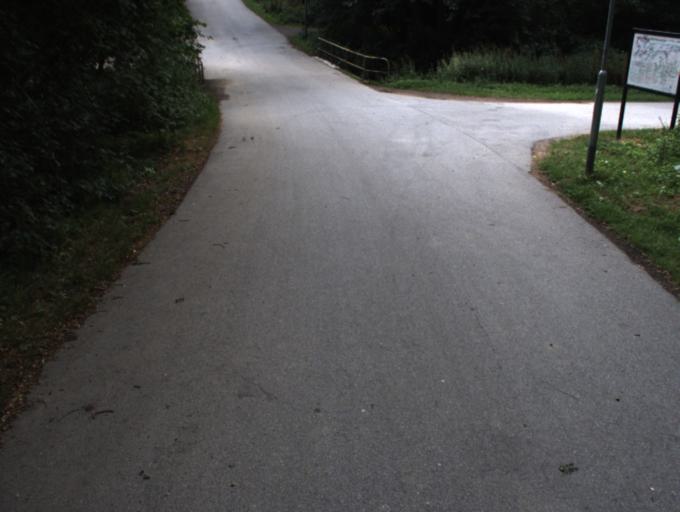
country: SE
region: Skane
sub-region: Helsingborg
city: Helsingborg
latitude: 56.0340
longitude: 12.7239
